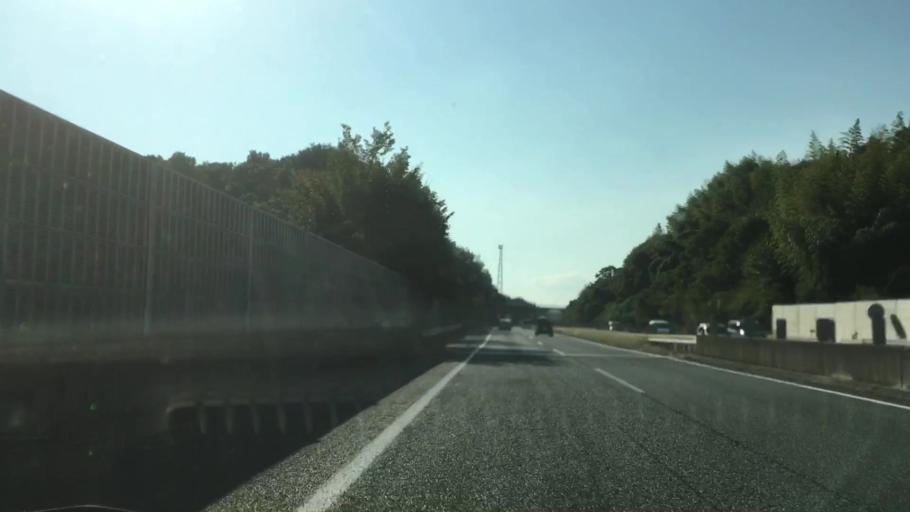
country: JP
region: Yamaguchi
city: Kudamatsu
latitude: 34.0421
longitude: 131.9070
